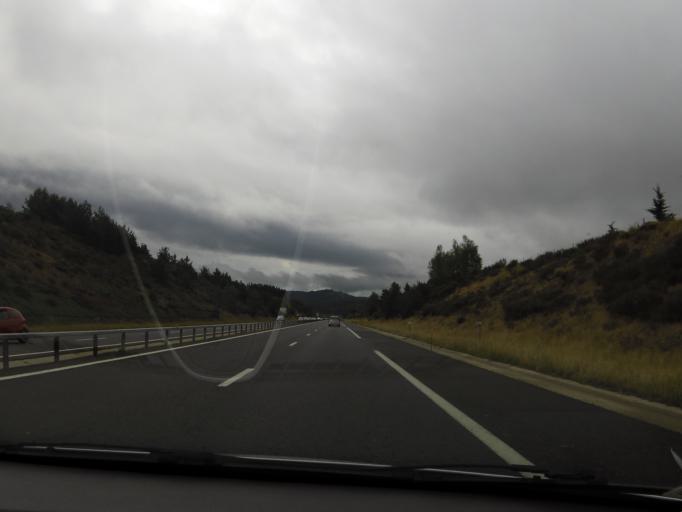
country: FR
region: Languedoc-Roussillon
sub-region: Departement de la Lozere
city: Aumont-Aubrac
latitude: 44.7619
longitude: 3.2842
